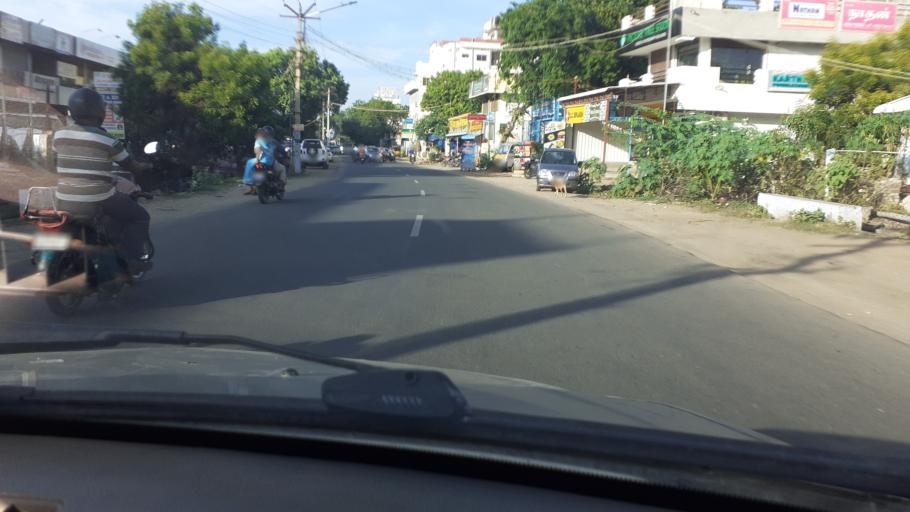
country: IN
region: Tamil Nadu
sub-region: Tirunelveli Kattabo
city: Tirunelveli
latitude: 8.7129
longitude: 77.7320
